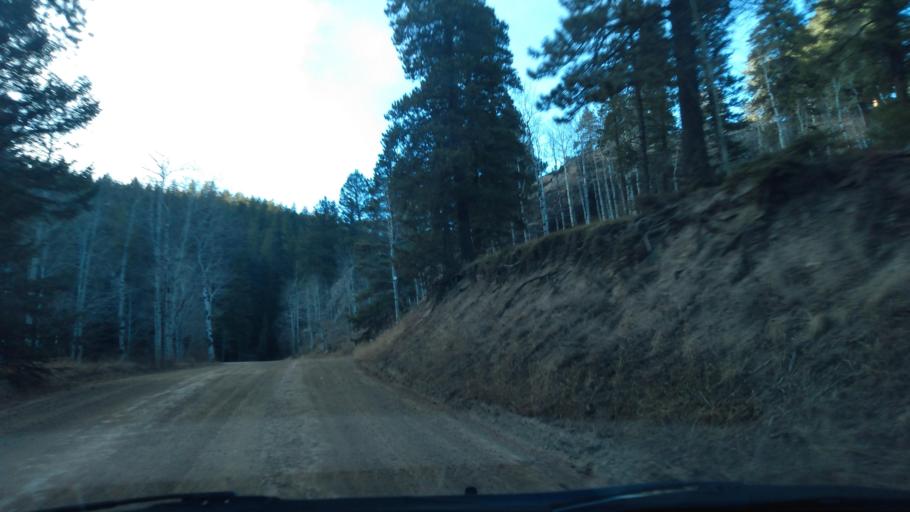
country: US
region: Colorado
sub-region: Boulder County
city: Nederland
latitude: 39.9429
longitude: -105.4438
